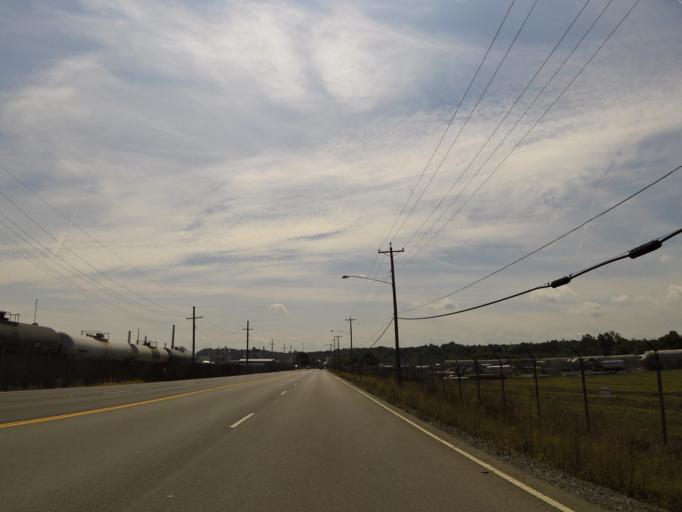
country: US
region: Tennessee
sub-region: Sullivan County
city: Kingsport
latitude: 36.5239
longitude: -82.5561
